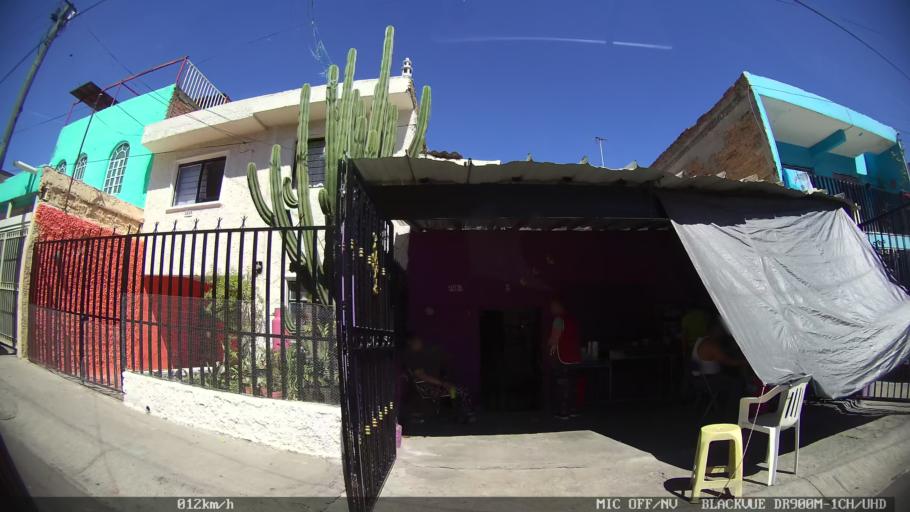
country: MX
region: Jalisco
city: Tlaquepaque
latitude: 20.6957
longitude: -103.2819
